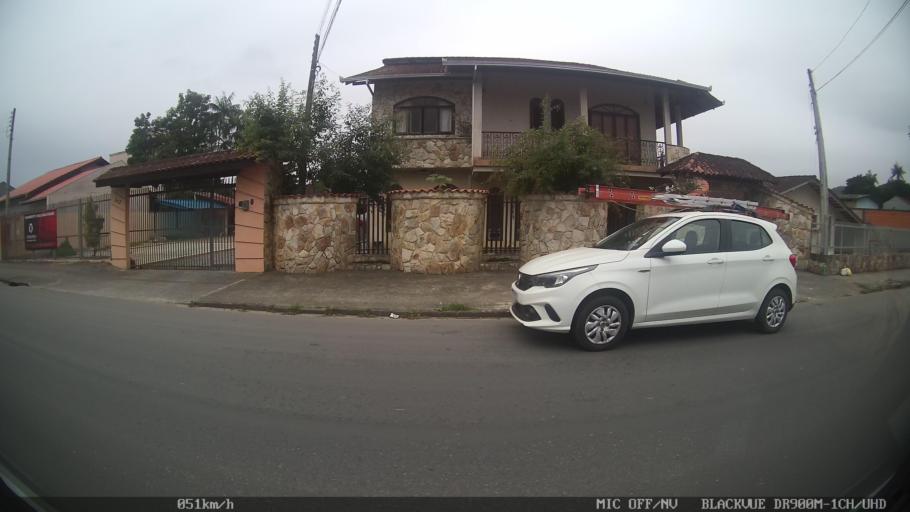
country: BR
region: Santa Catarina
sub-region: Joinville
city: Joinville
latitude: -26.2685
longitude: -48.8198
